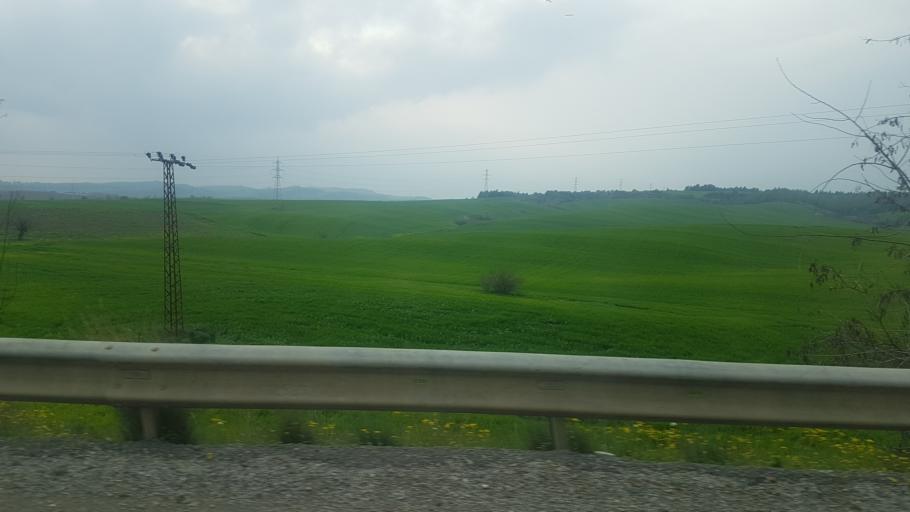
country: TR
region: Mersin
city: Yenice
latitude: 37.0681
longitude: 35.1723
